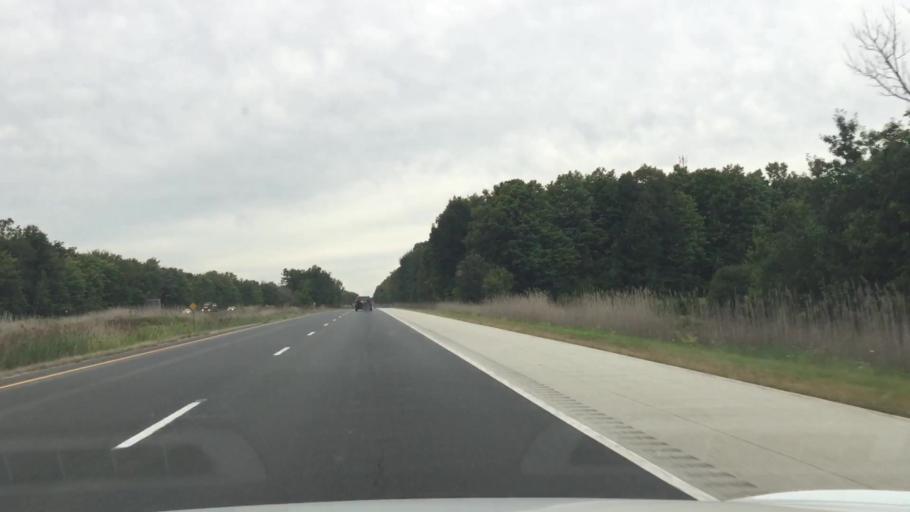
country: CA
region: Ontario
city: Camlachie
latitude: 42.9915
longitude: -82.0191
